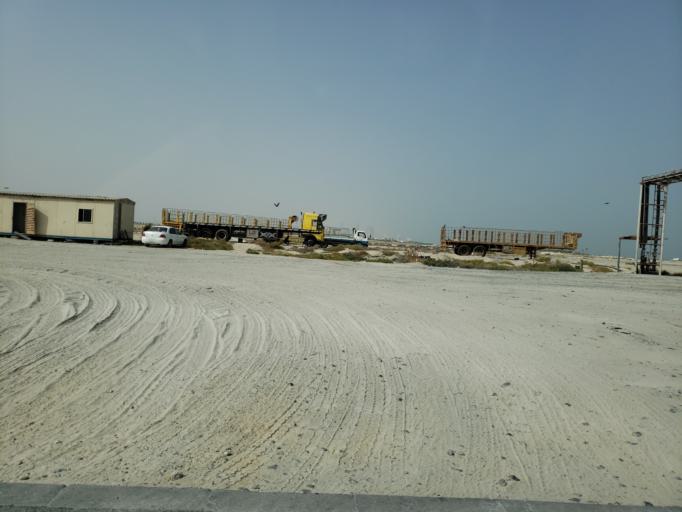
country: AE
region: Ajman
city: Ajman
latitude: 25.4458
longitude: 55.4733
